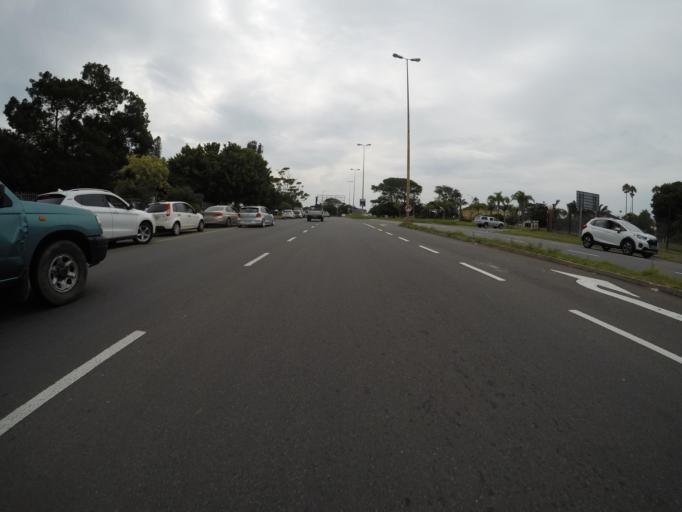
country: ZA
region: Eastern Cape
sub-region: Buffalo City Metropolitan Municipality
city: East London
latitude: -32.9947
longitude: 27.8966
